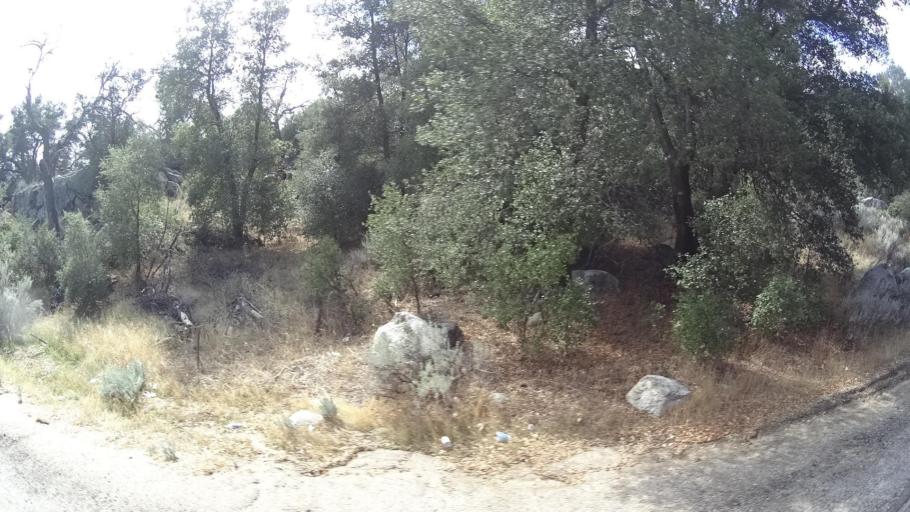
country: US
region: California
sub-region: San Diego County
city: Campo
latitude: 32.7086
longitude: -116.4915
